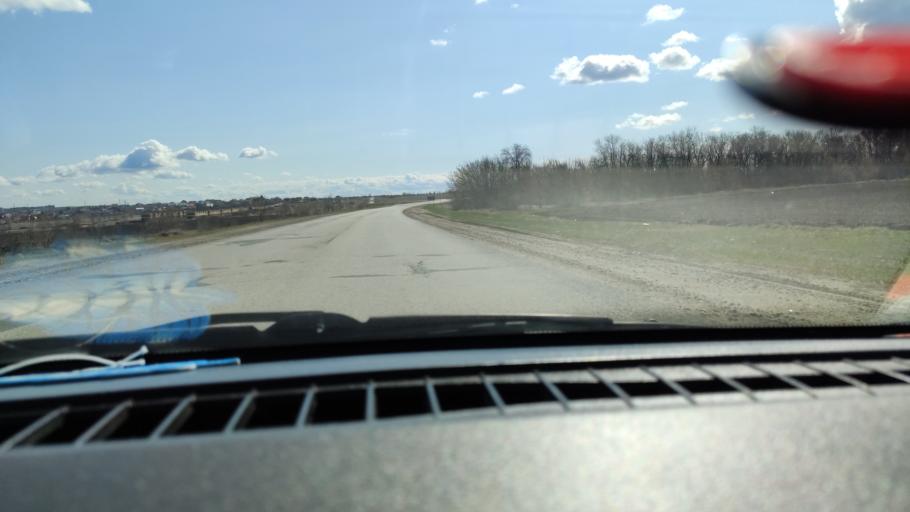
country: RU
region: Samara
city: Varlamovo
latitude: 53.1152
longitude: 48.3480
